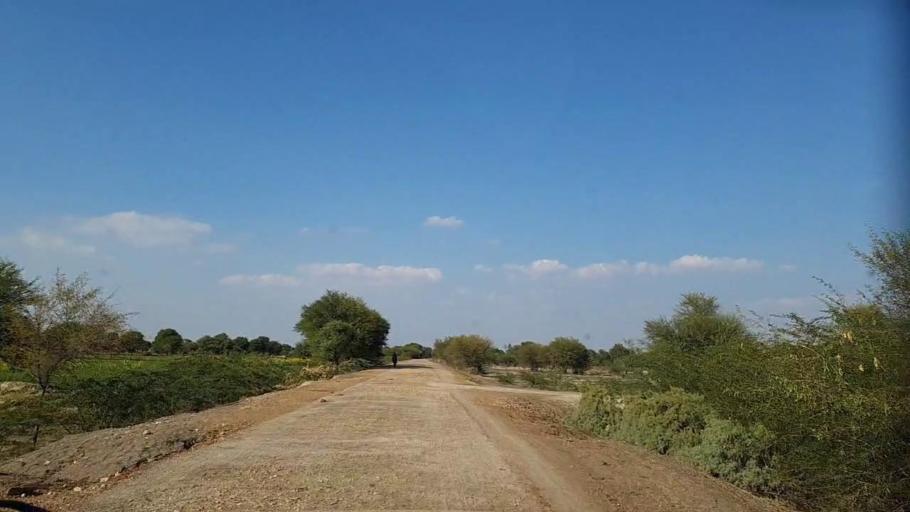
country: PK
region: Sindh
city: Pithoro
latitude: 25.6344
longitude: 69.3513
